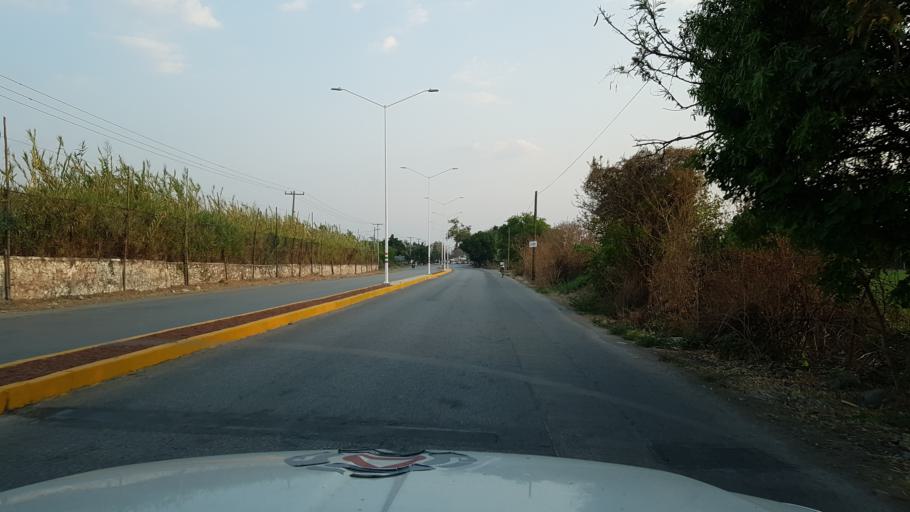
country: MX
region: Morelos
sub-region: Ayala
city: Olintepec
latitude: 18.7462
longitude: -98.9858
